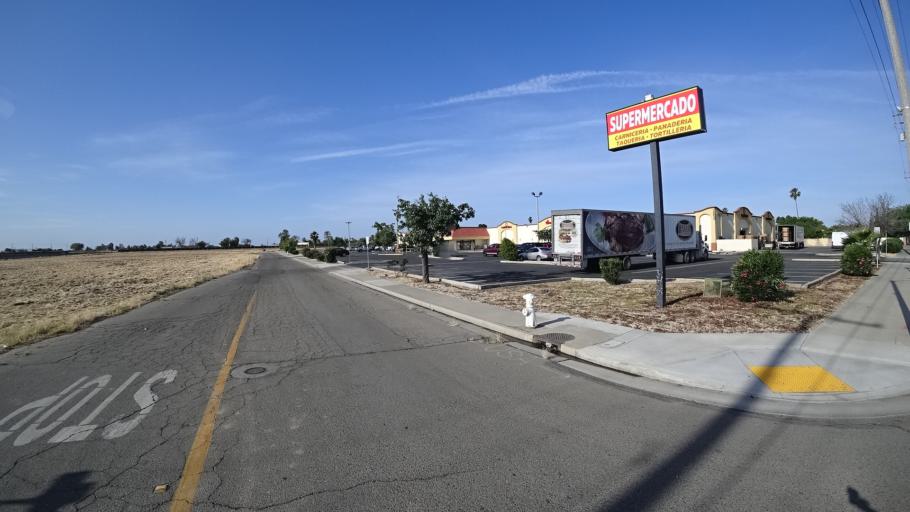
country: US
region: California
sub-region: Kings County
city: Hanford
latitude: 36.3133
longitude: -119.6505
